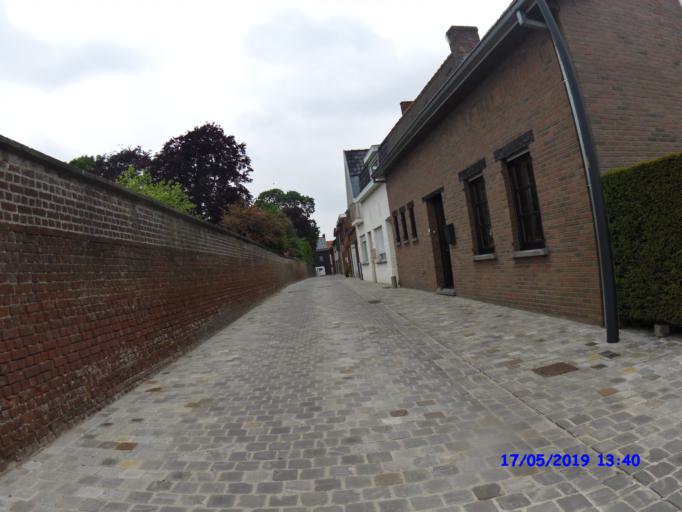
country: BE
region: Flanders
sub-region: Provincie West-Vlaanderen
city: Wielsbeke
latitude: 50.9094
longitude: 3.3896
